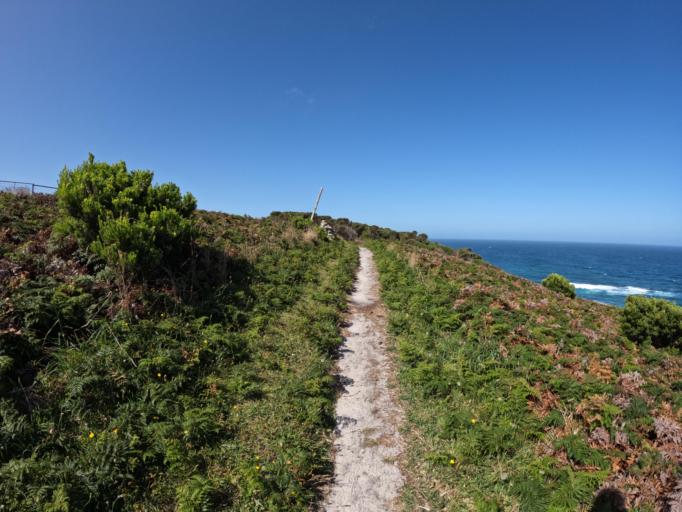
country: AU
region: Victoria
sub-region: Colac-Otway
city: Apollo Bay
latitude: -38.7903
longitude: 143.6454
